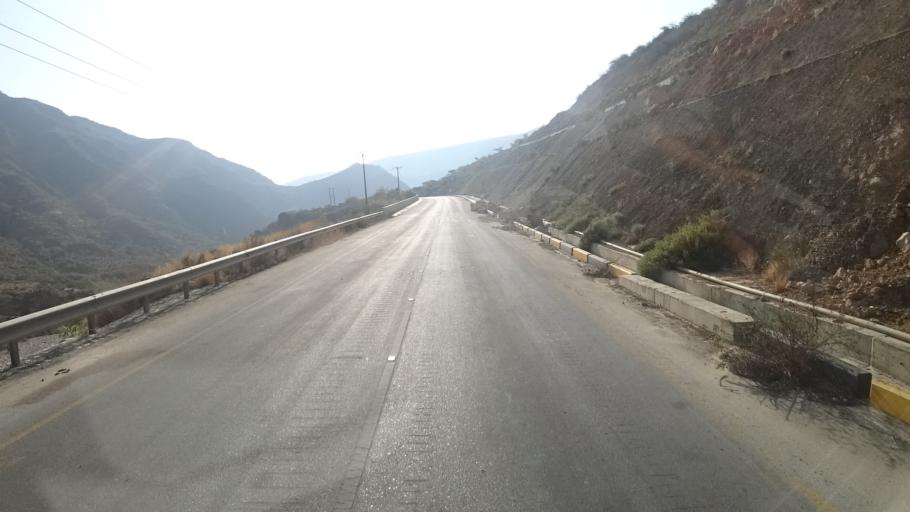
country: YE
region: Al Mahrah
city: Hawf
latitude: 16.7482
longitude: 53.2262
